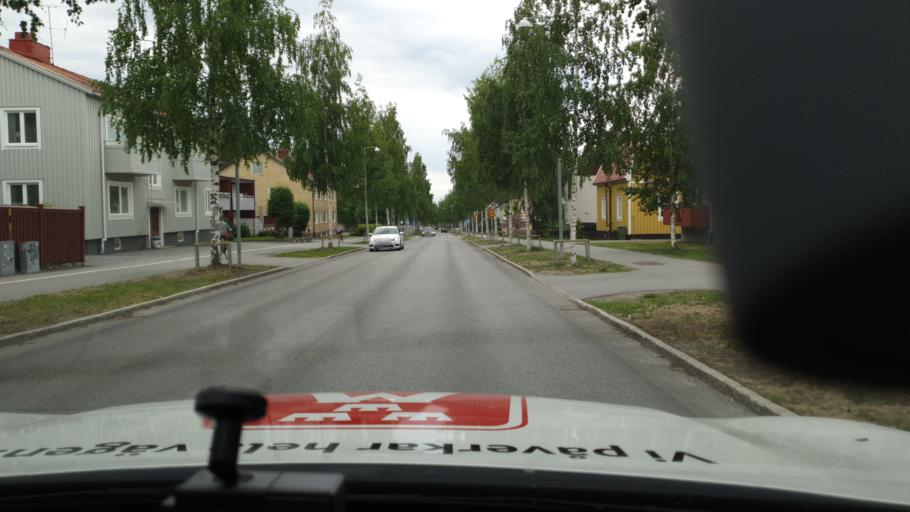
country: SE
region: Vaesterbotten
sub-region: Umea Kommun
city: Umea
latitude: 63.8435
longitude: 20.2887
